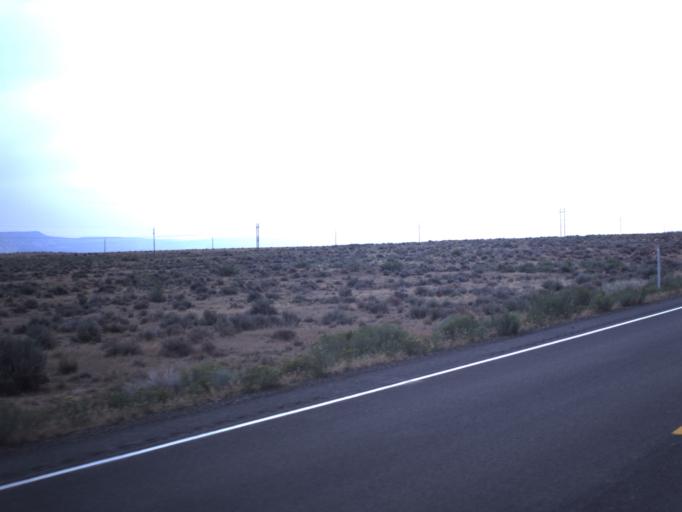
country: US
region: Utah
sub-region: Uintah County
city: Naples
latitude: 40.2257
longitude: -109.3984
